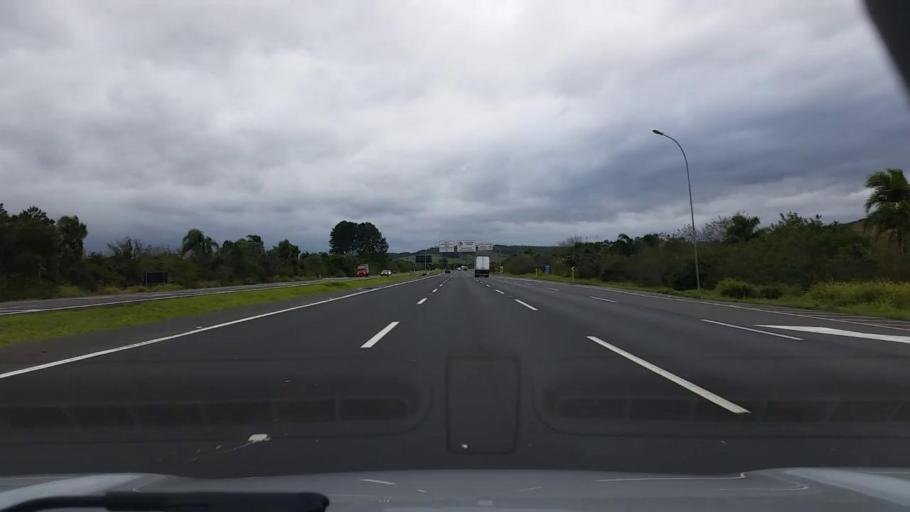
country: BR
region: Rio Grande do Sul
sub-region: Osorio
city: Osorio
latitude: -29.8869
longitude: -50.4529
